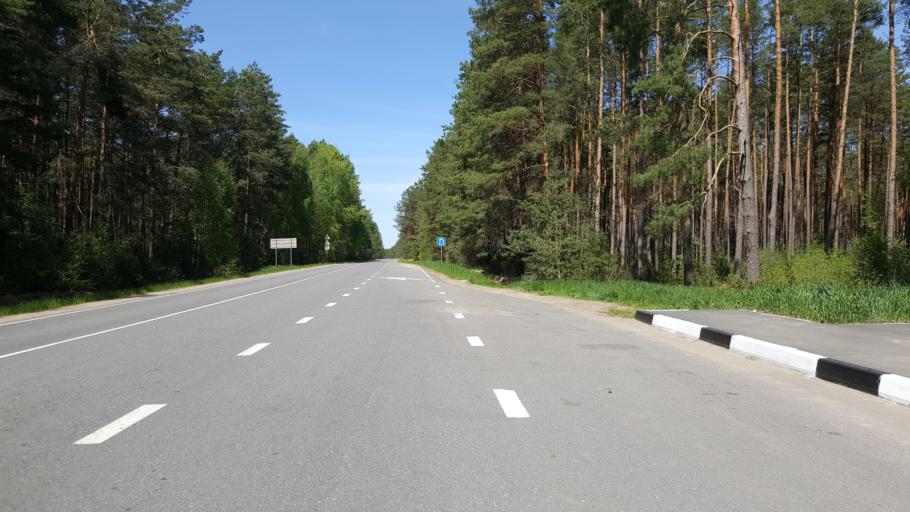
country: BY
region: Brest
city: Zhabinka
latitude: 52.3801
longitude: 24.1218
